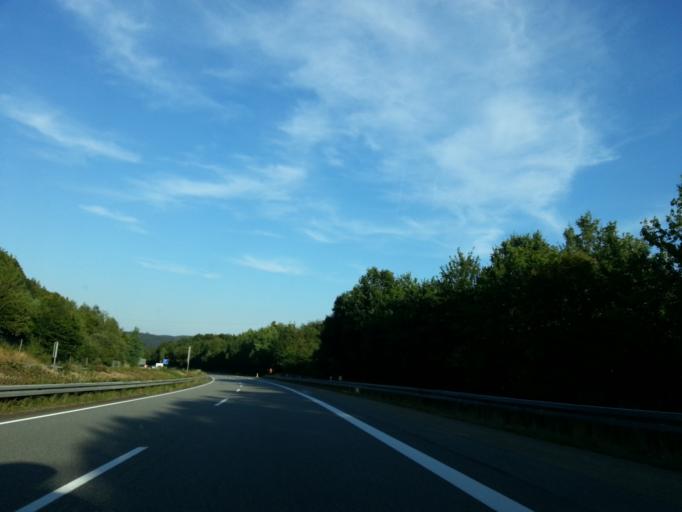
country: DE
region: Rheinland-Pfalz
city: Achtelsbach
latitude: 49.5896
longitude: 7.0604
